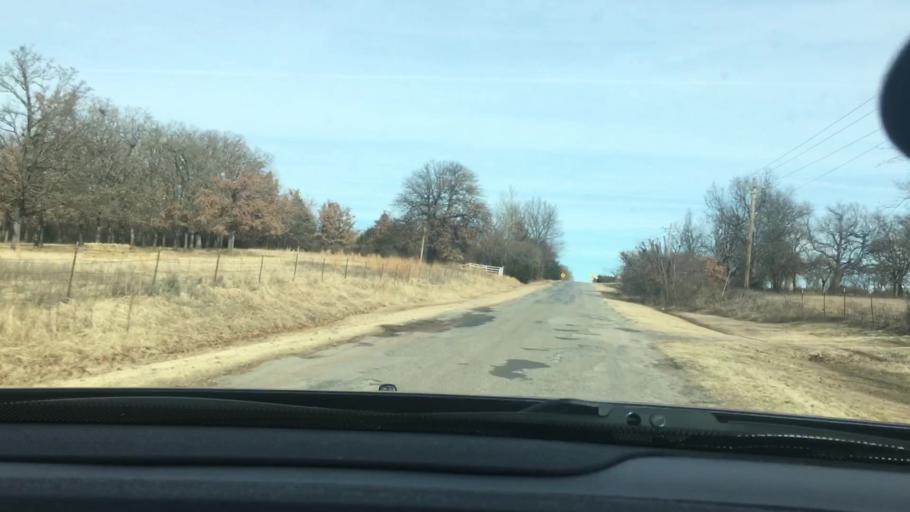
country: US
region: Oklahoma
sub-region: Garvin County
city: Wynnewood
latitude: 34.6473
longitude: -97.2476
